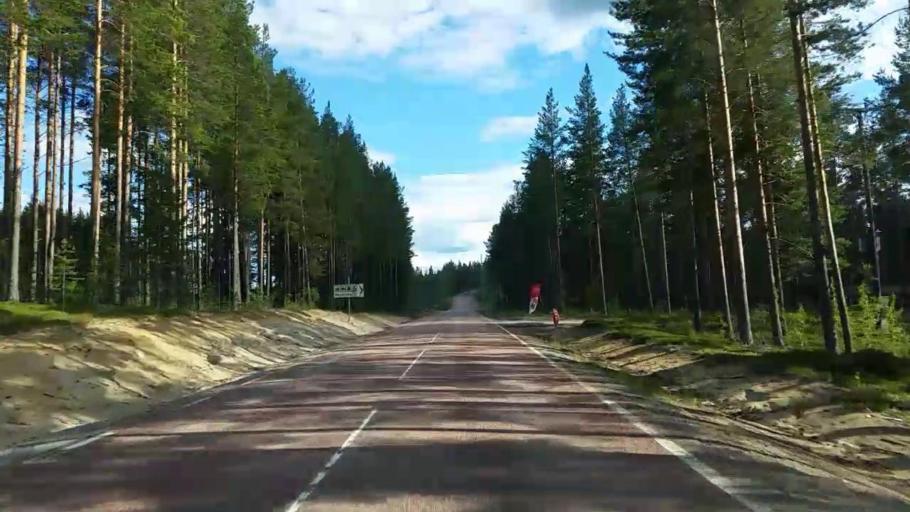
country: SE
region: Gaevleborg
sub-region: Ljusdals Kommun
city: Farila
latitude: 62.0170
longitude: 15.9069
